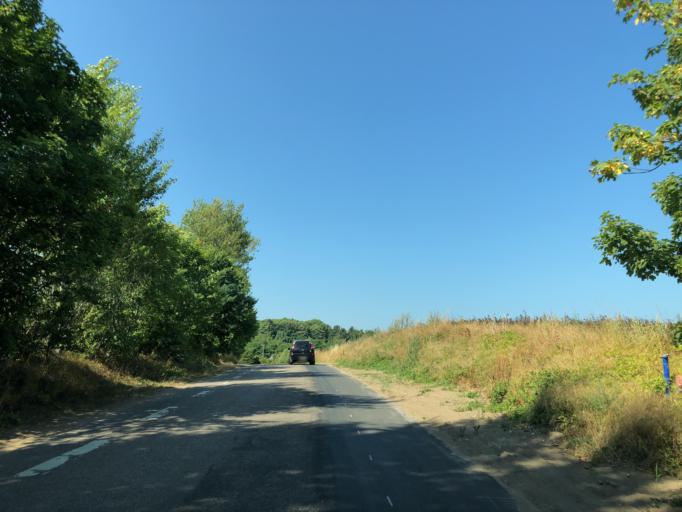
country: DK
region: Capital Region
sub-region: Halsnaes Kommune
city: Hundested
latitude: 55.9756
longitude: 11.9069
